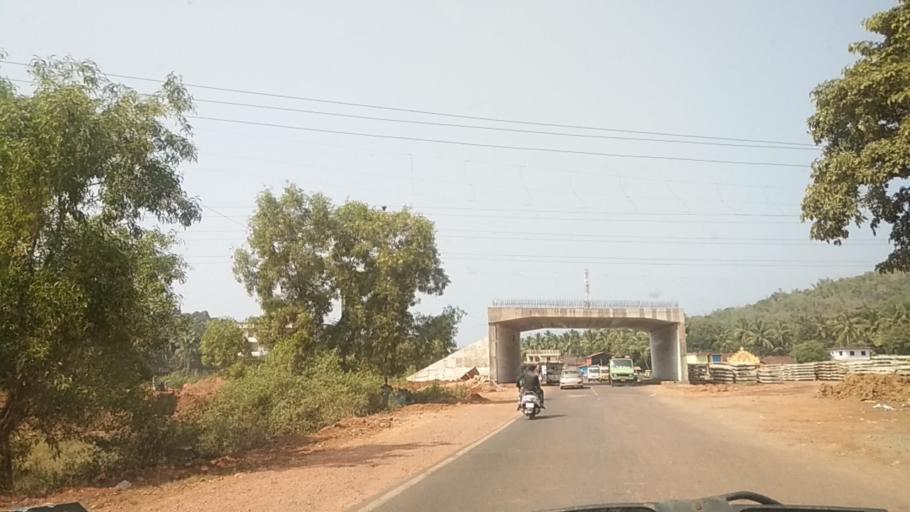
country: IN
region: Goa
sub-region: South Goa
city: Kankon
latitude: 15.0106
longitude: 74.0380
